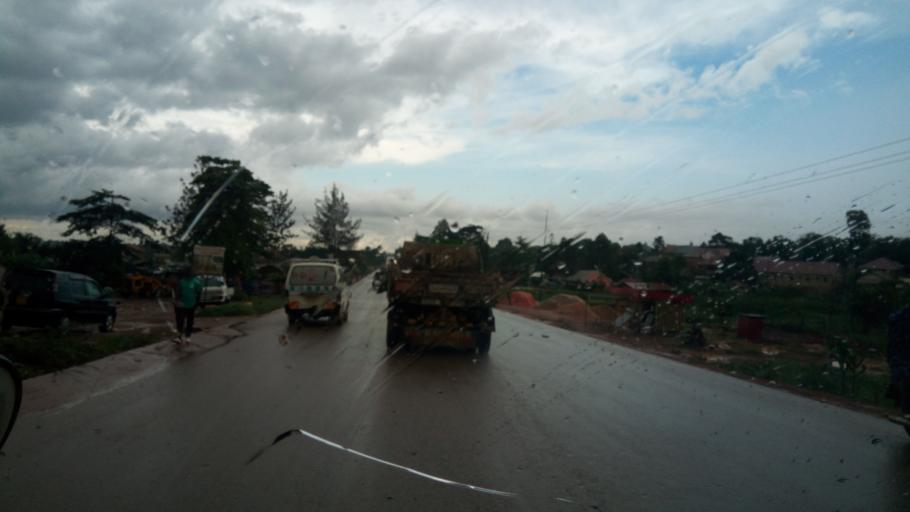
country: UG
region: Central Region
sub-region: Wakiso District
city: Wakiso
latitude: 0.3977
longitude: 32.4833
